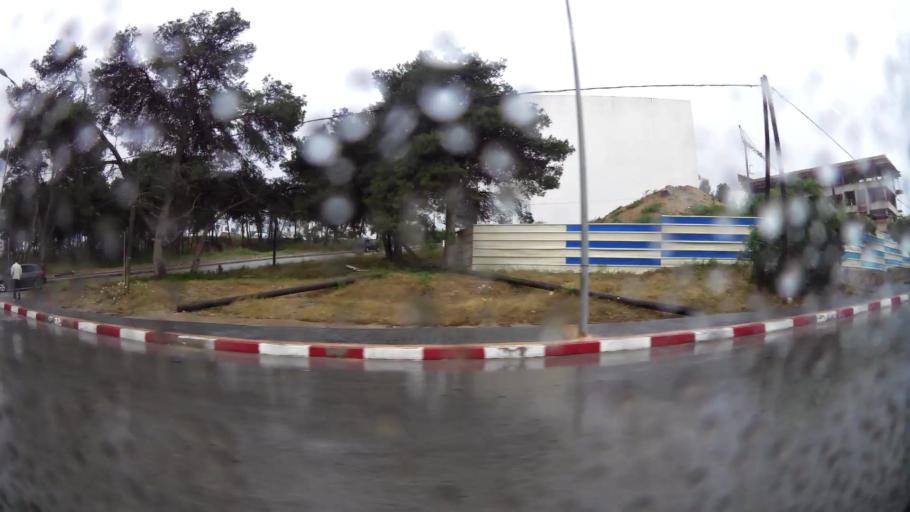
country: MA
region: Taza-Al Hoceima-Taounate
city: Al Hoceima
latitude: 35.2477
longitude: -3.9395
